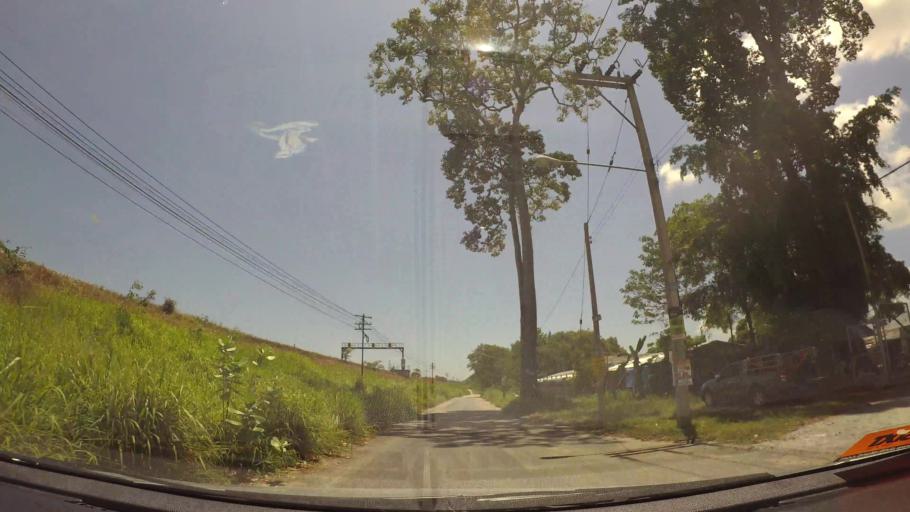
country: TH
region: Chon Buri
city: Si Racha
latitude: 13.1271
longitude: 100.9447
